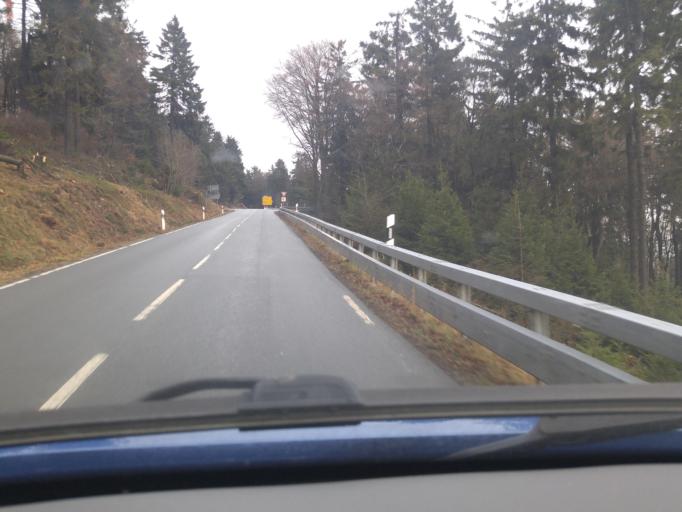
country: DE
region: Hesse
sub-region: Regierungsbezirk Darmstadt
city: Schmitten
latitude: 50.2301
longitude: 8.4575
